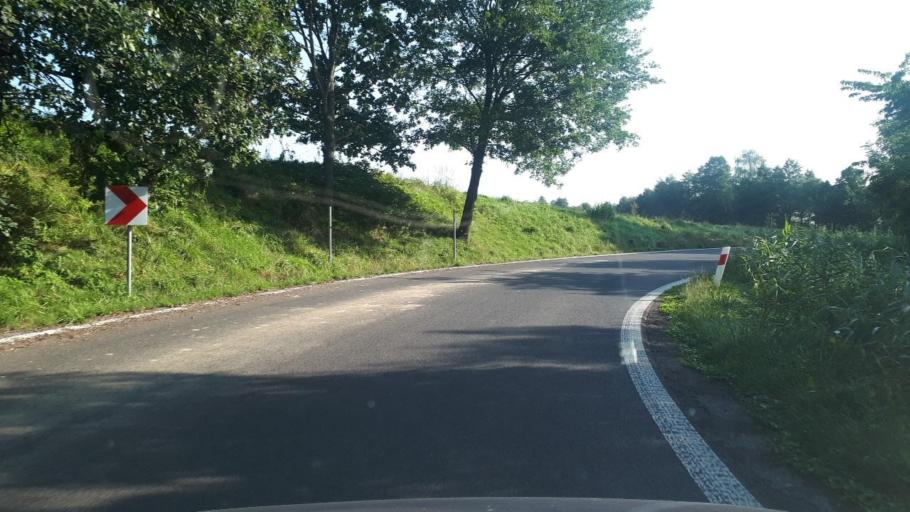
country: PL
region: Silesian Voivodeship
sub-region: Powiat cieszynski
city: Piersciec
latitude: 49.8568
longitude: 18.8410
